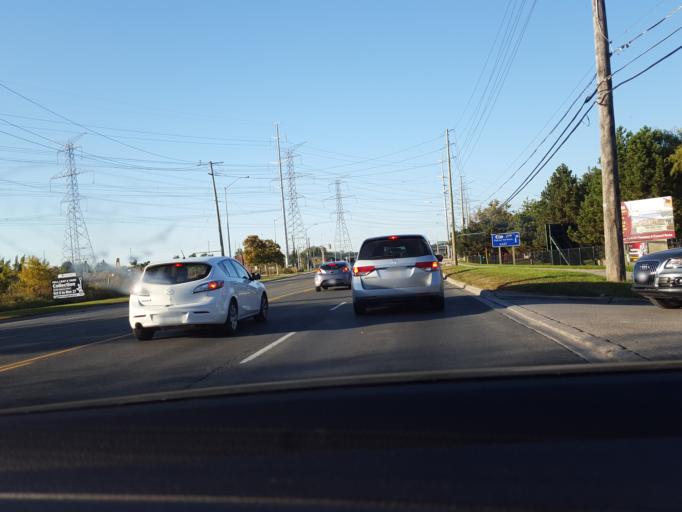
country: CA
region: Ontario
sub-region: York
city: Richmond Hill
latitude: 43.8308
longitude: -79.4278
